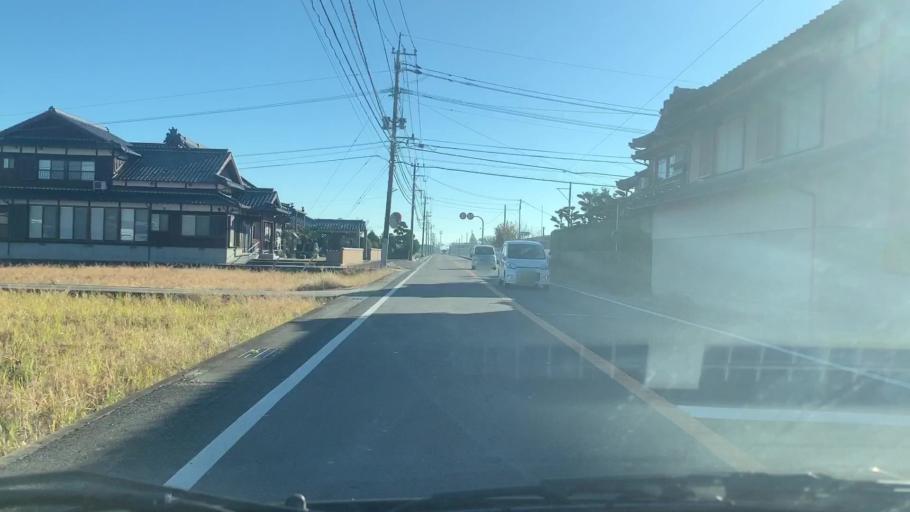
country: JP
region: Saga Prefecture
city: Kashima
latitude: 33.1841
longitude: 130.1654
